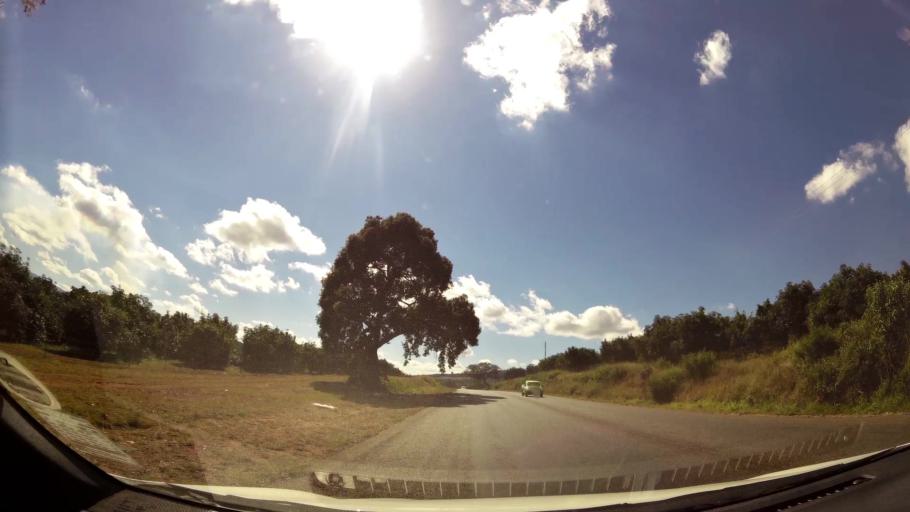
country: ZA
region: Limpopo
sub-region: Mopani District Municipality
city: Tzaneen
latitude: -23.8058
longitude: 30.1774
